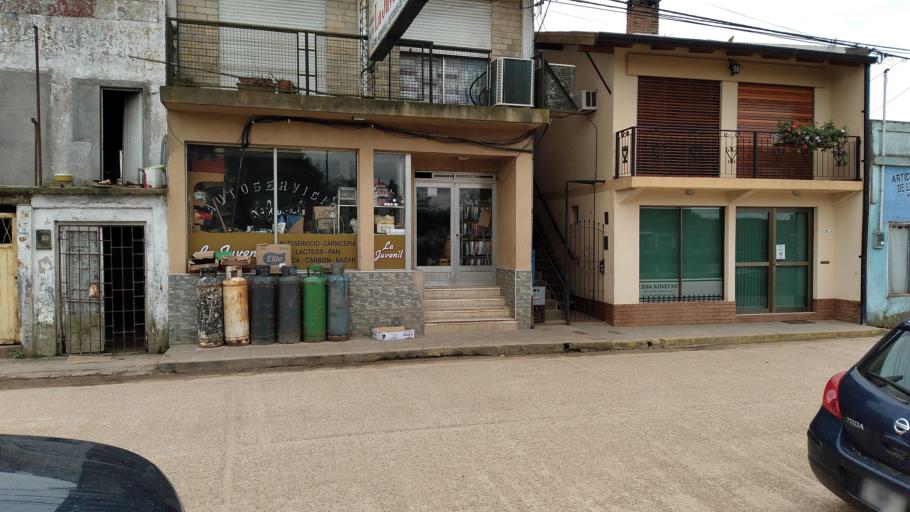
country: AR
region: Entre Rios
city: Villa Paranacito
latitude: -33.7166
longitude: -58.6574
